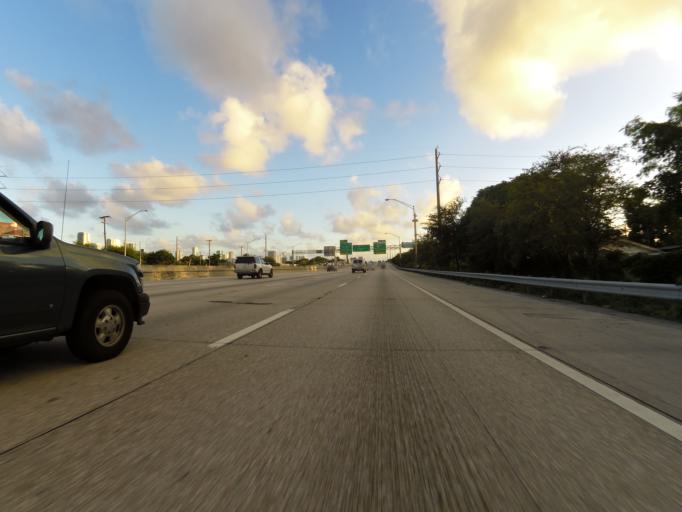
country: US
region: Florida
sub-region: Miami-Dade County
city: Allapattah
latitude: 25.7989
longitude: -80.2059
